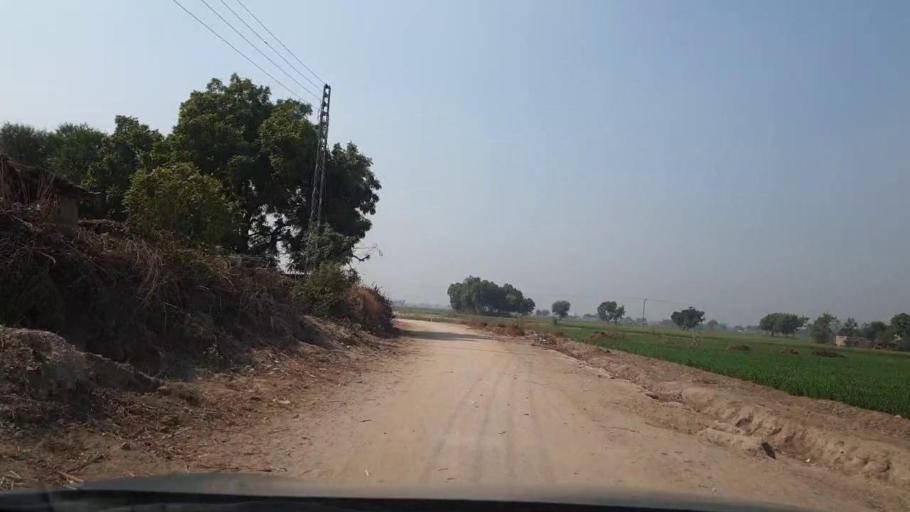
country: PK
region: Sindh
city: Tando Allahyar
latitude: 25.4984
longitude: 68.7697
